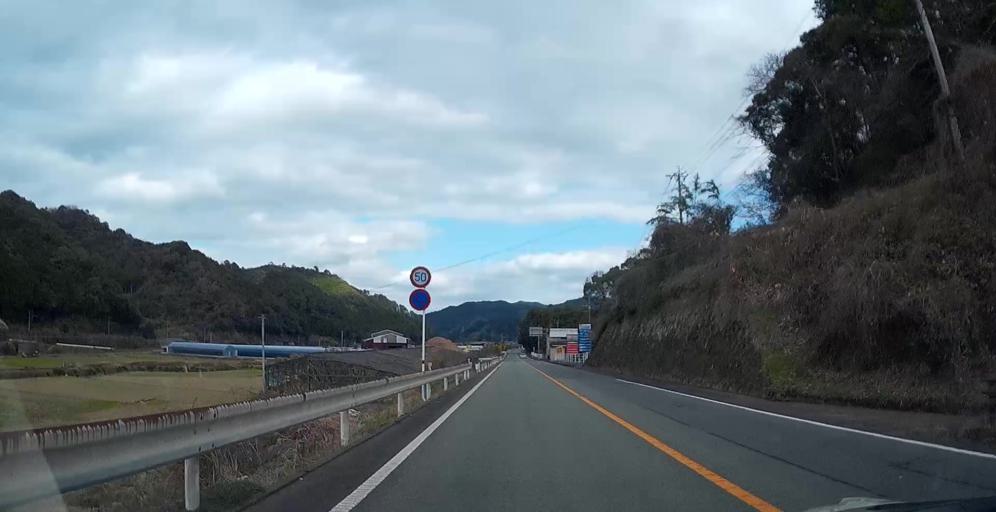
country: JP
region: Kumamoto
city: Minamata
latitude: 32.3385
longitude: 130.4929
